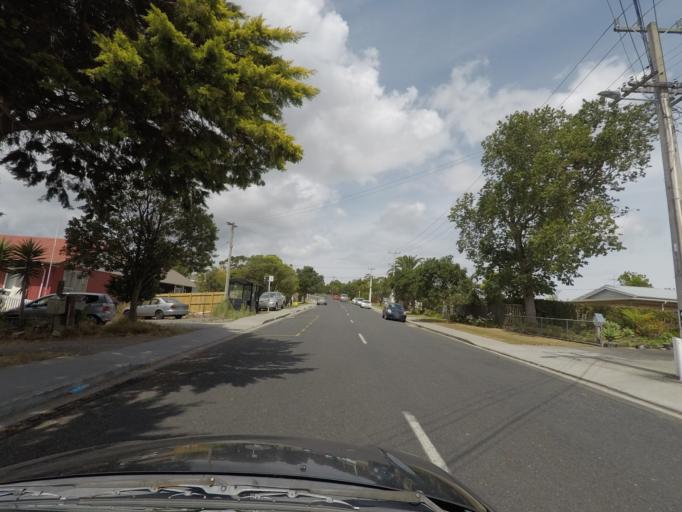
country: NZ
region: Auckland
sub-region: Auckland
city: Waitakere
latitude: -36.9000
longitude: 174.6403
